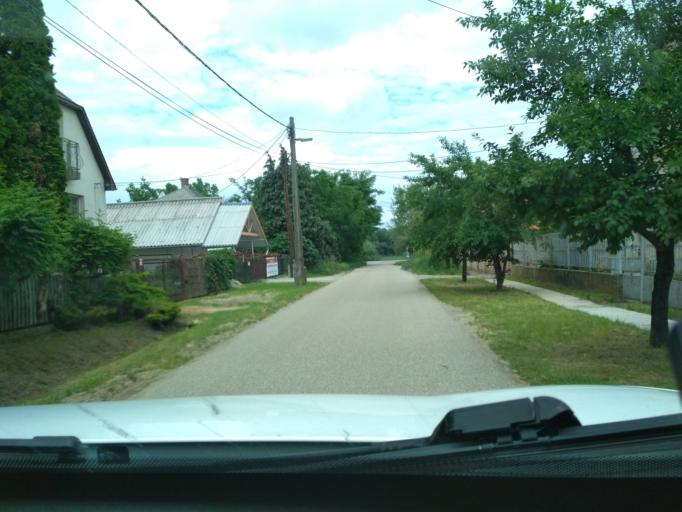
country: HU
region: Jasz-Nagykun-Szolnok
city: Tiszafured
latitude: 47.6080
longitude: 20.7234
